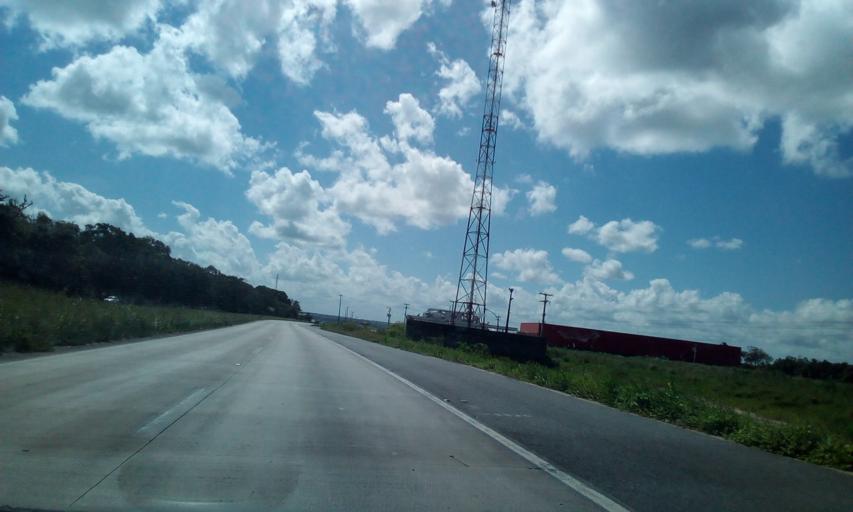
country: BR
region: Pernambuco
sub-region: Itapissuma
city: Itapissuma
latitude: -7.7950
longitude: -34.9277
